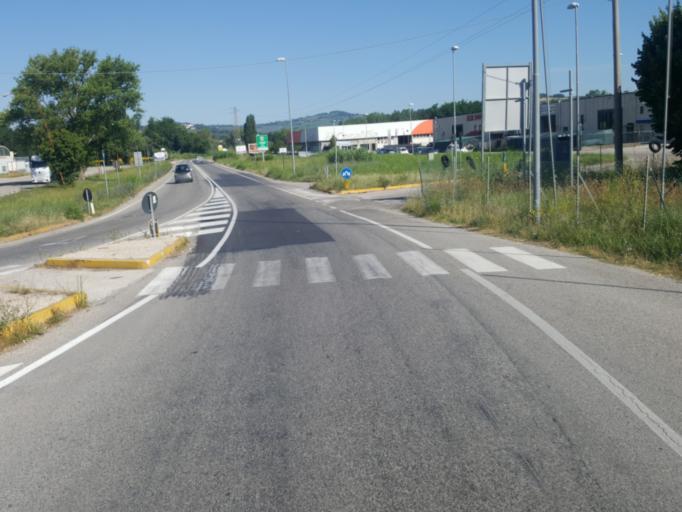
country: IT
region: The Marches
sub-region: Provincia di Pesaro e Urbino
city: Borgo Santa Maria
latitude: 43.8639
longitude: 12.8143
